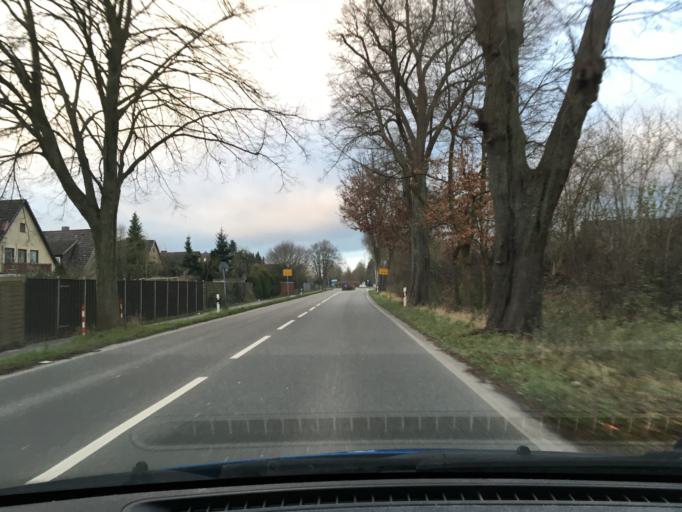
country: DE
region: Lower Saxony
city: Uelzen
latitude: 52.9559
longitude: 10.5799
